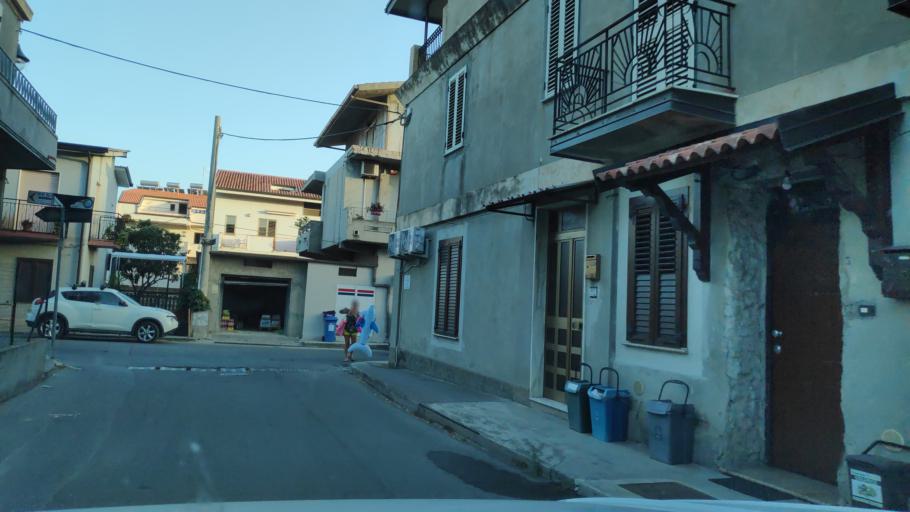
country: IT
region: Calabria
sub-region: Provincia di Reggio Calabria
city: Bova Marina
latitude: 37.9297
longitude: 15.9113
